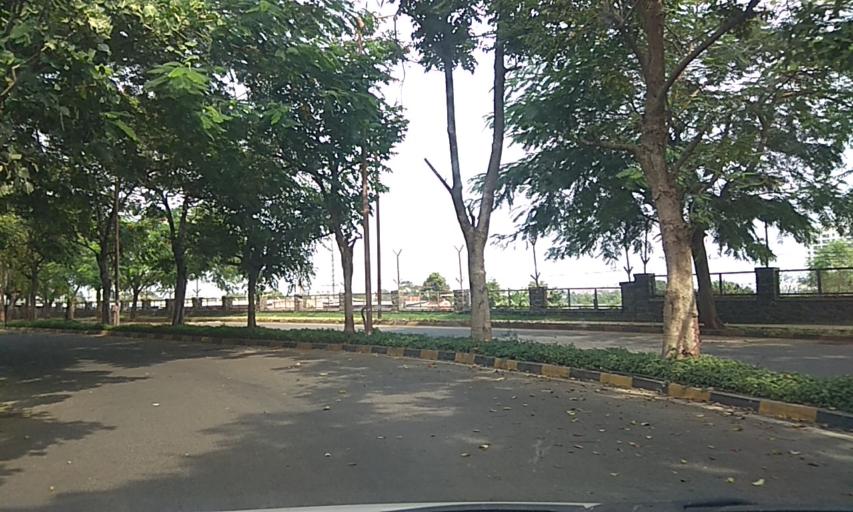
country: IN
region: Maharashtra
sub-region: Pune Division
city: Pimpri
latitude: 18.6025
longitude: 73.7168
